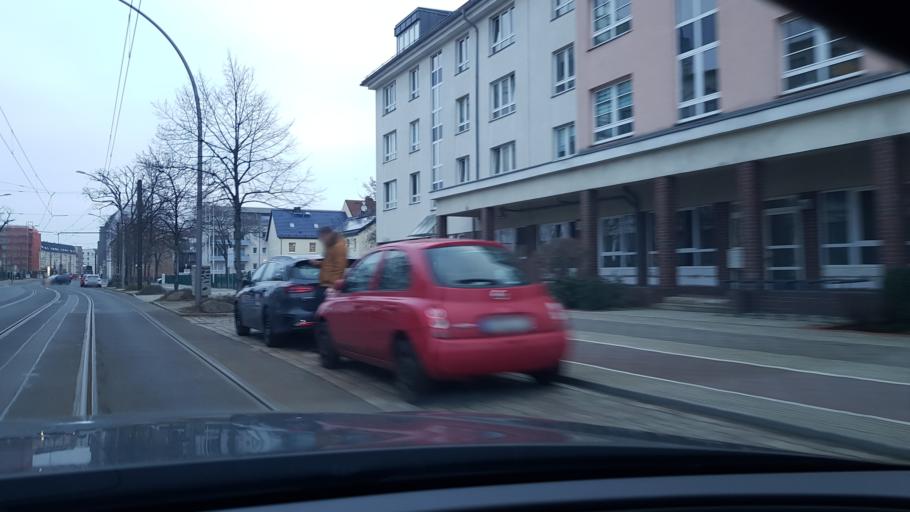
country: DE
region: Berlin
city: Berlin Koepenick
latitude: 52.4376
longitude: 13.5822
